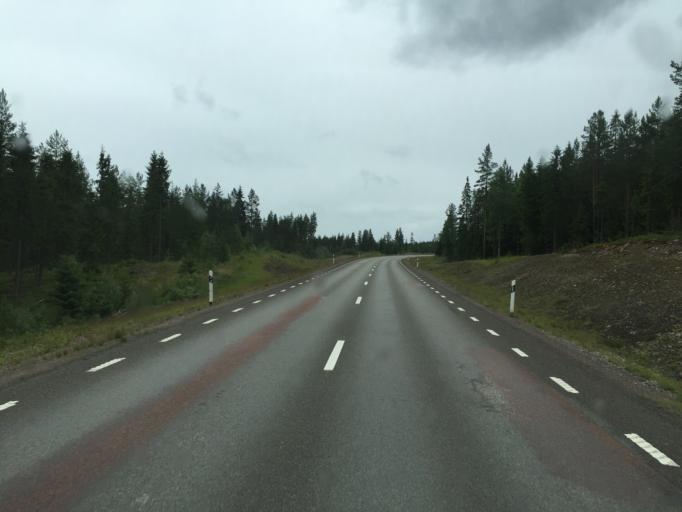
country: SE
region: Dalarna
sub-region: Malung-Saelens kommun
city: Malung
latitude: 60.5958
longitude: 13.5790
